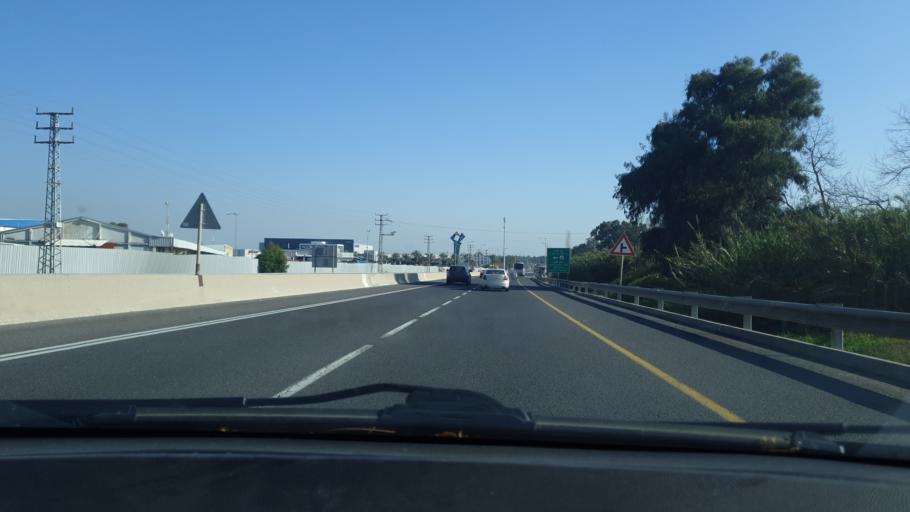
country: IL
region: Central District
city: Kefar Habad
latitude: 31.9669
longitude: 34.8460
